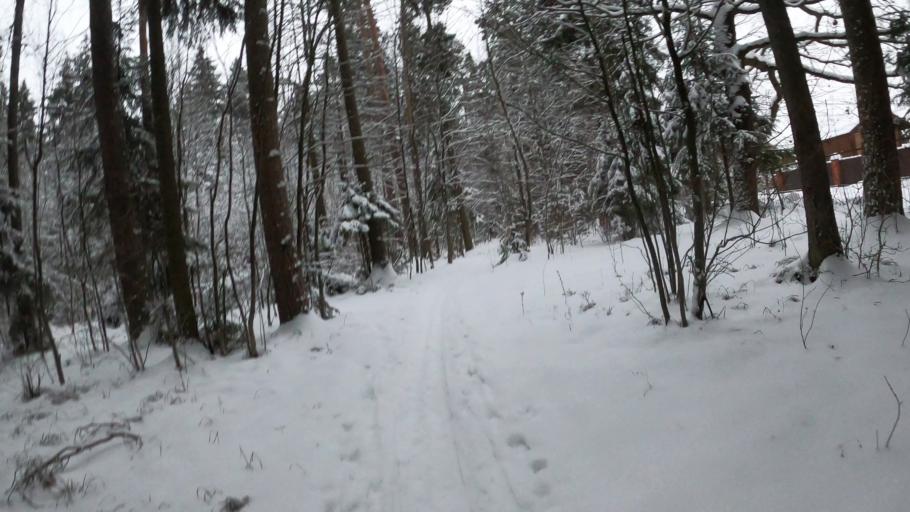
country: RU
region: Moskovskaya
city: Firsanovka
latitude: 55.9149
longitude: 37.2044
